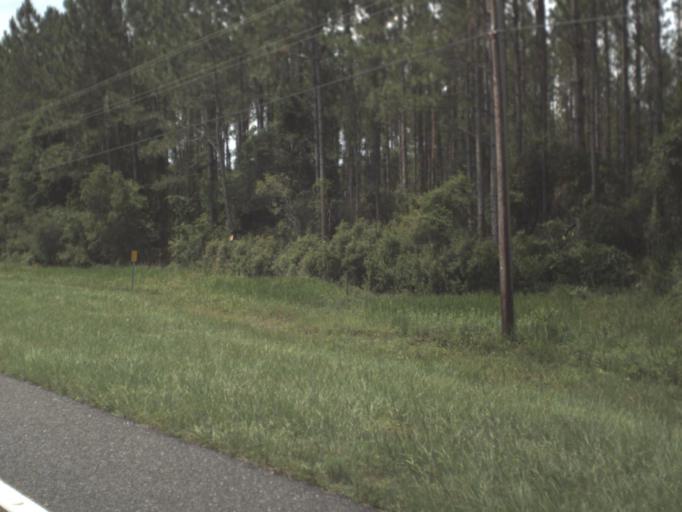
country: US
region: Florida
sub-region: Levy County
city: Chiefland
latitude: 29.4154
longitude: -82.8225
